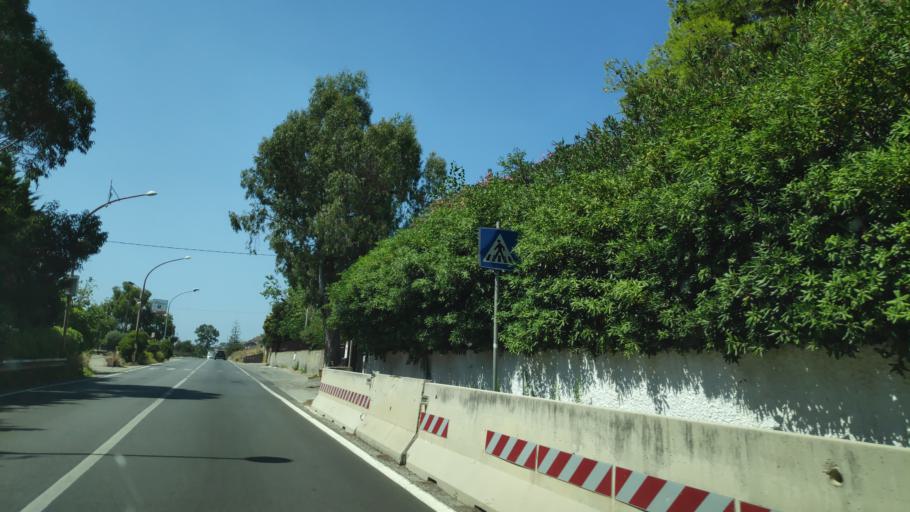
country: IT
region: Calabria
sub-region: Provincia di Reggio Calabria
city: Weather Station
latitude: 37.9575
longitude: 16.0957
